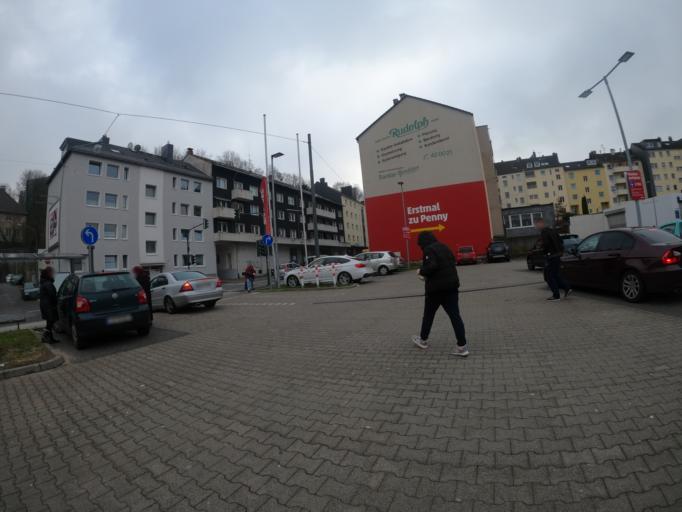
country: DE
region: North Rhine-Westphalia
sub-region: Regierungsbezirk Dusseldorf
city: Wuppertal
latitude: 51.2468
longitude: 7.1430
